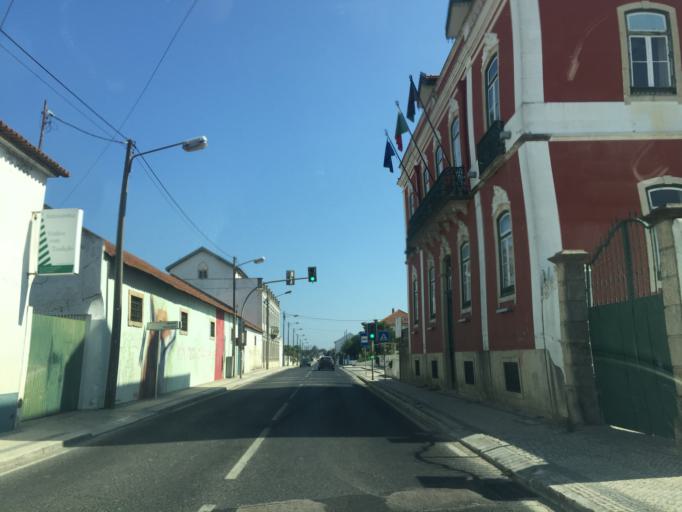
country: PT
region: Santarem
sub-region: Alpiarca
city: Alpiarca
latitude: 39.2645
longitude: -8.5794
